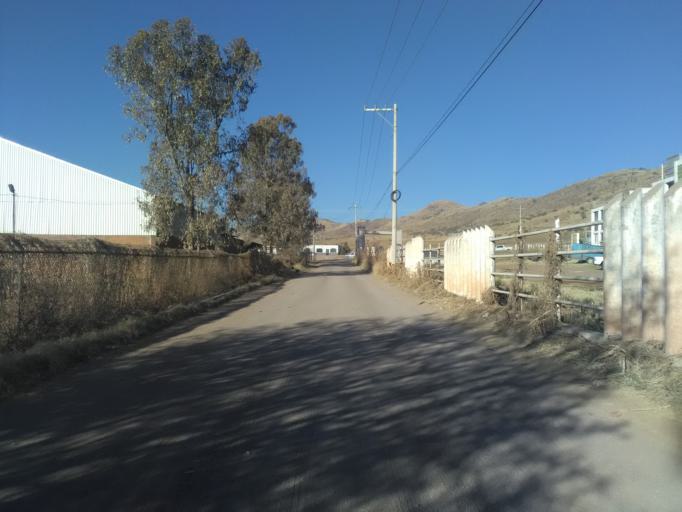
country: MX
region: Durango
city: Victoria de Durango
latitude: 24.0622
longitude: -104.6544
